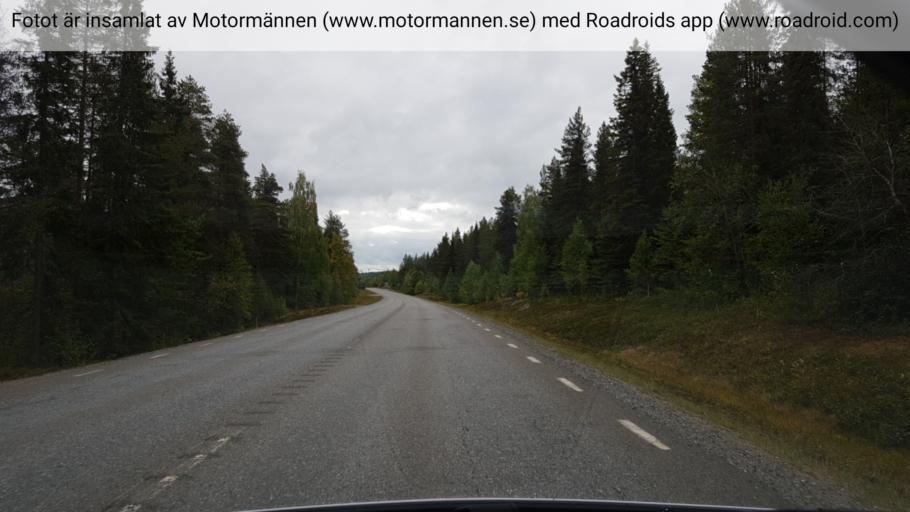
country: SE
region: Vaesterbotten
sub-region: Skelleftea Kommun
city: Boliden
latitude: 64.8879
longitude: 20.3800
